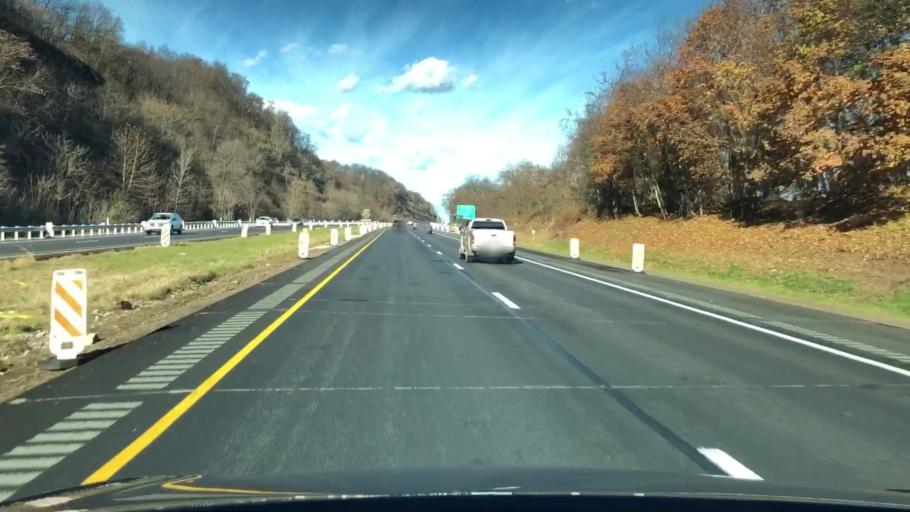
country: US
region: Pennsylvania
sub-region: Allegheny County
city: Tarentum
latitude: 40.5978
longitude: -79.7695
